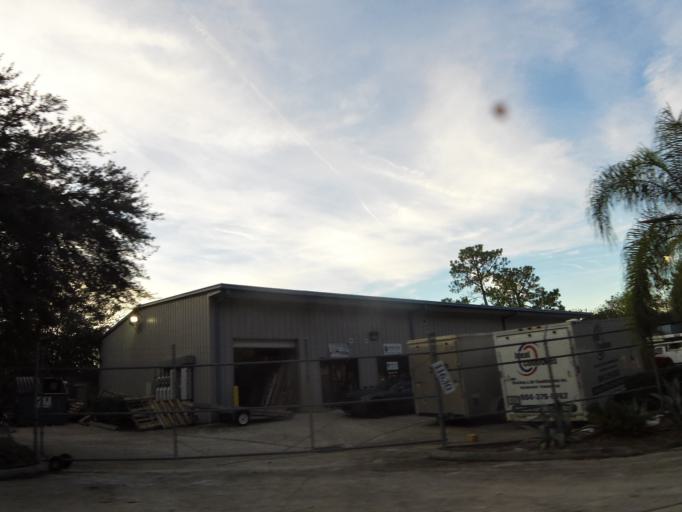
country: US
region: Florida
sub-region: Saint Johns County
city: Fruit Cove
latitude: 30.1553
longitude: -81.5370
